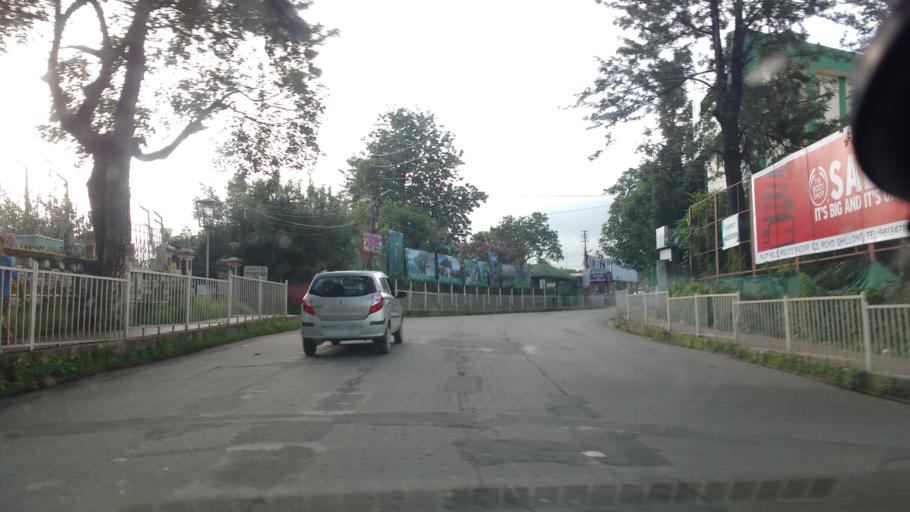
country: IN
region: Meghalaya
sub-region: East Khasi Hills
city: Shillong
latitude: 25.5753
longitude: 91.8841
